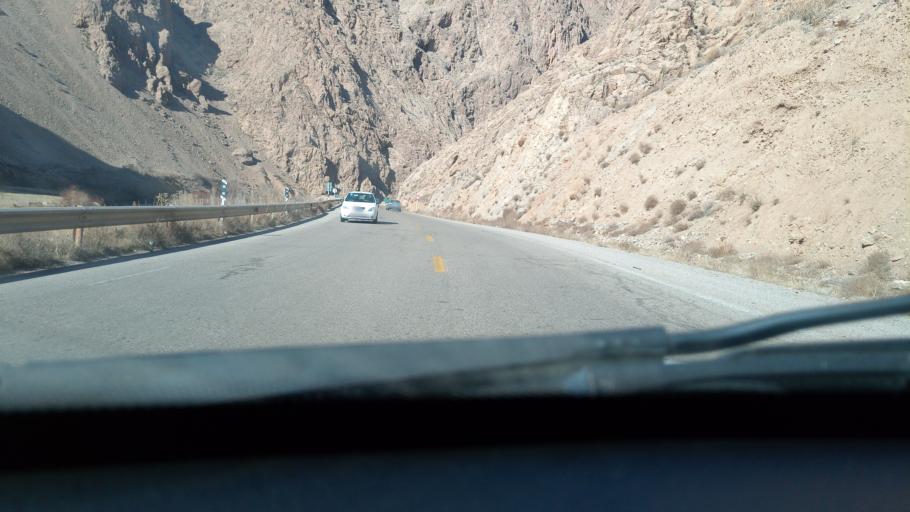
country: IR
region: Khorasan-e Shomali
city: Esfarayen
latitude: 37.1766
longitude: 57.4165
